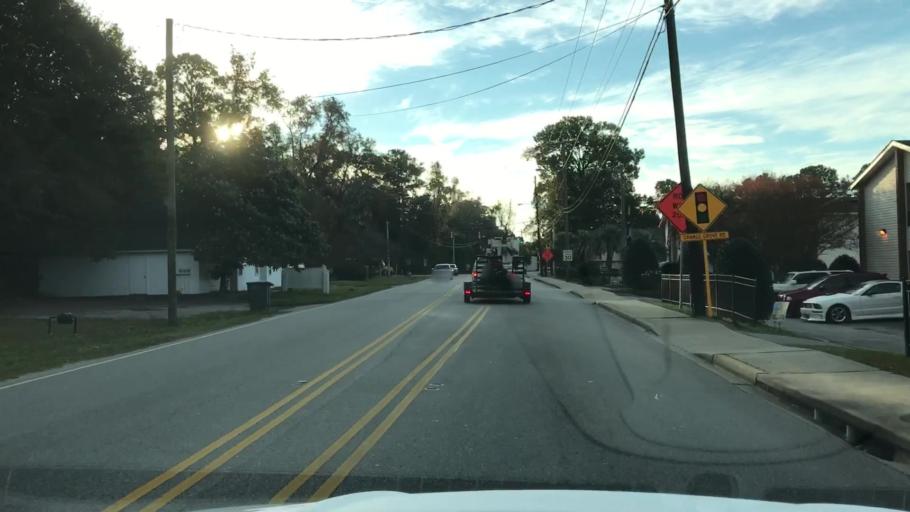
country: US
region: South Carolina
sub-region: Charleston County
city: North Charleston
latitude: 32.8113
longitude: -80.0114
